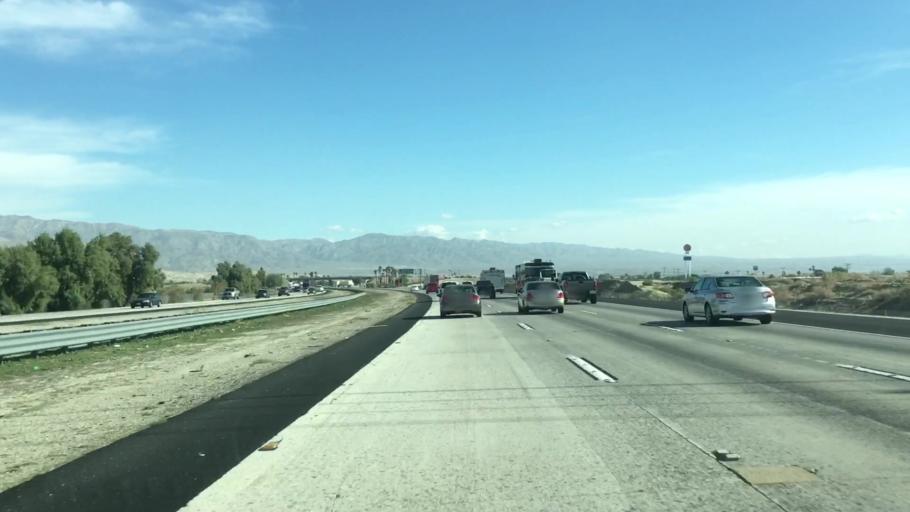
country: US
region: California
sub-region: Riverside County
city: Indio
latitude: 33.7381
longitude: -116.2427
